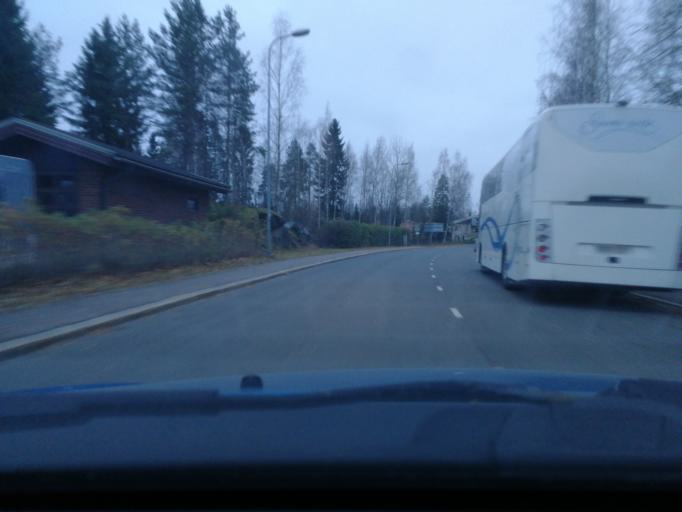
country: FI
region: Pirkanmaa
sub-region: Tampere
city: Tampere
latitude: 61.4439
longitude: 23.8729
